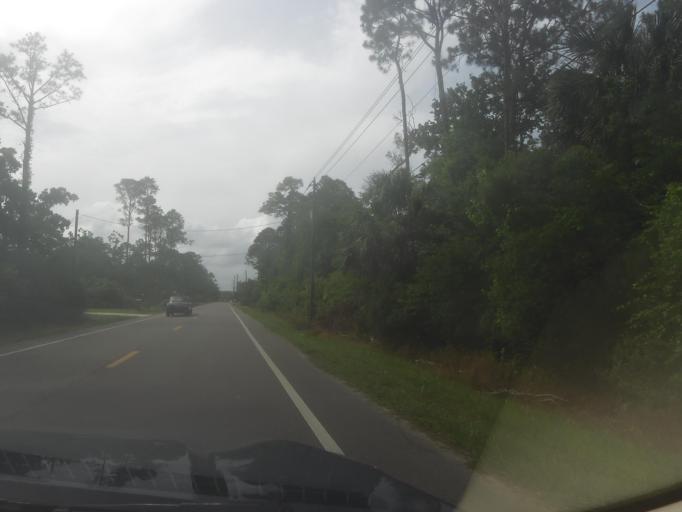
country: US
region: Florida
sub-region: Saint Johns County
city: Saint Augustine
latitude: 29.9003
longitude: -81.3489
